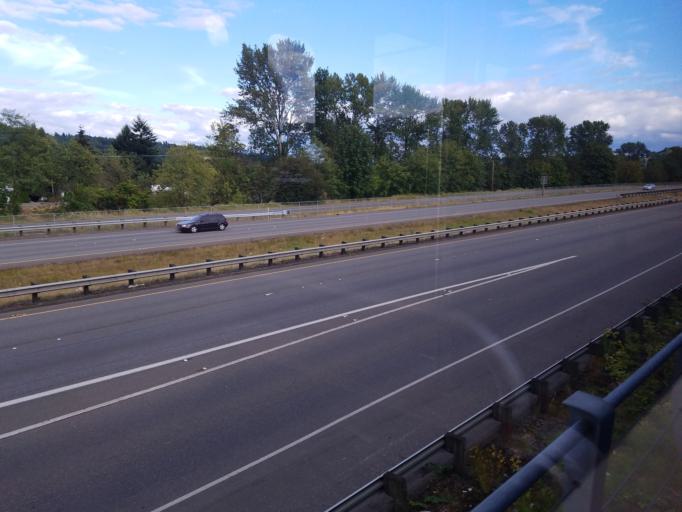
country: US
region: Washington
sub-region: King County
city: Riverton
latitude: 47.4934
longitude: -122.2824
